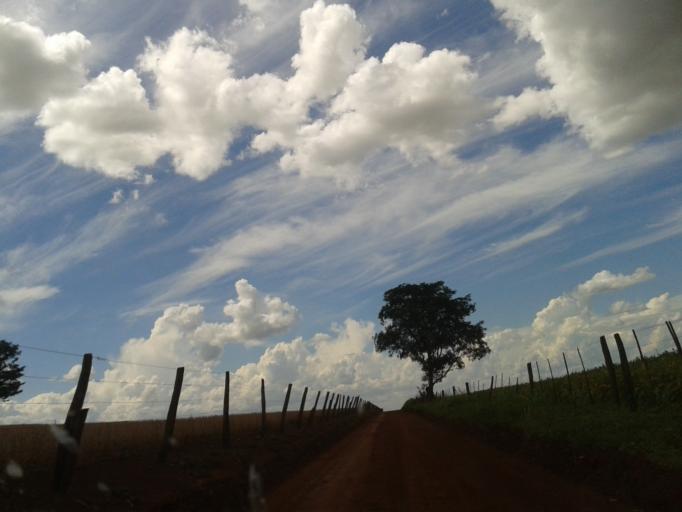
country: BR
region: Minas Gerais
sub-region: Capinopolis
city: Capinopolis
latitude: -18.7199
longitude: -49.7701
